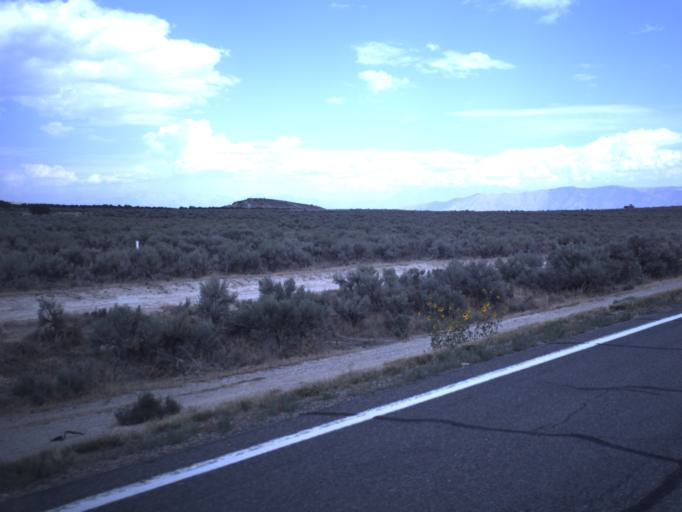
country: US
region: Utah
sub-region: Utah County
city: Eagle Mountain
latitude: 40.2311
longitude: -112.1864
